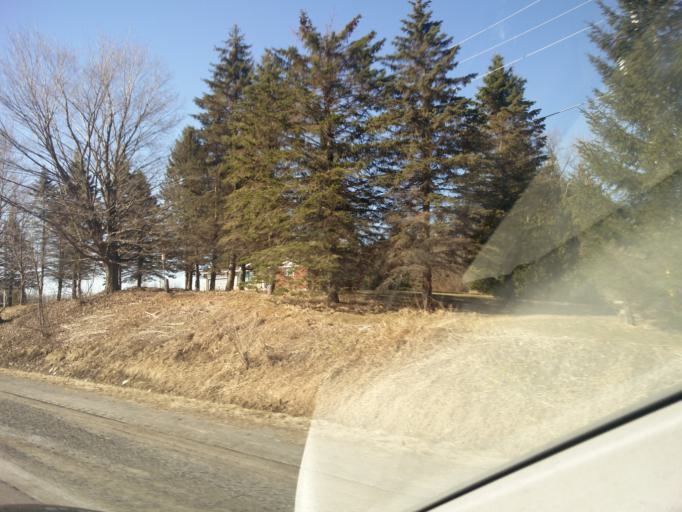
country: CA
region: Ontario
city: Bells Corners
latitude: 45.1855
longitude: -75.7226
